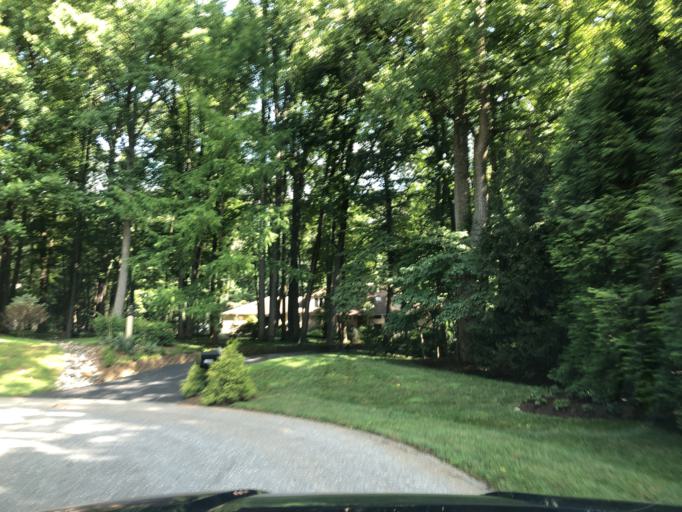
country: US
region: Maryland
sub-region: Howard County
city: Highland
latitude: 39.2058
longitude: -76.9716
